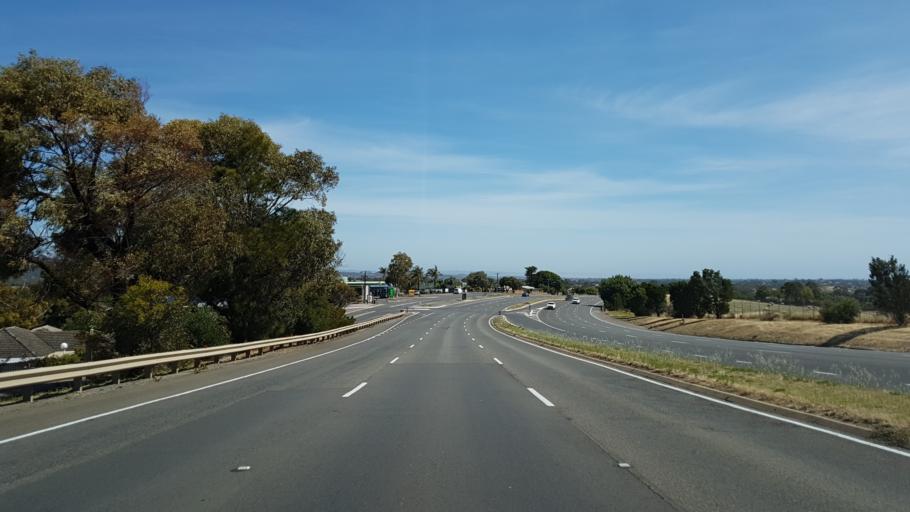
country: AU
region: South Australia
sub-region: Marion
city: Trott Park
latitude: -35.0693
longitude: 138.5546
